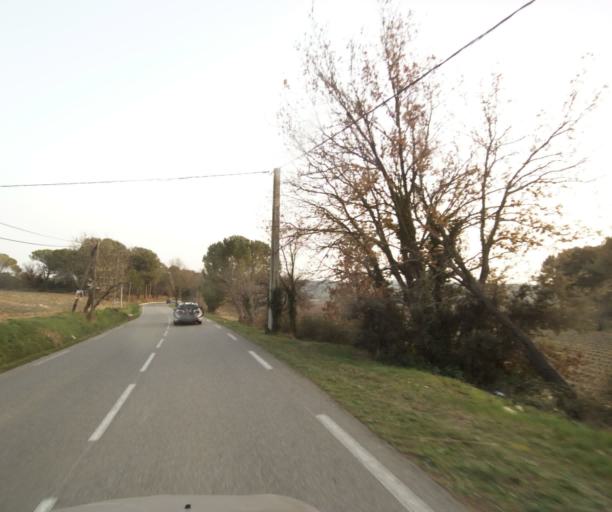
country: FR
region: Provence-Alpes-Cote d'Azur
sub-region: Departement des Bouches-du-Rhone
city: Eguilles
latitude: 43.5931
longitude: 5.3667
